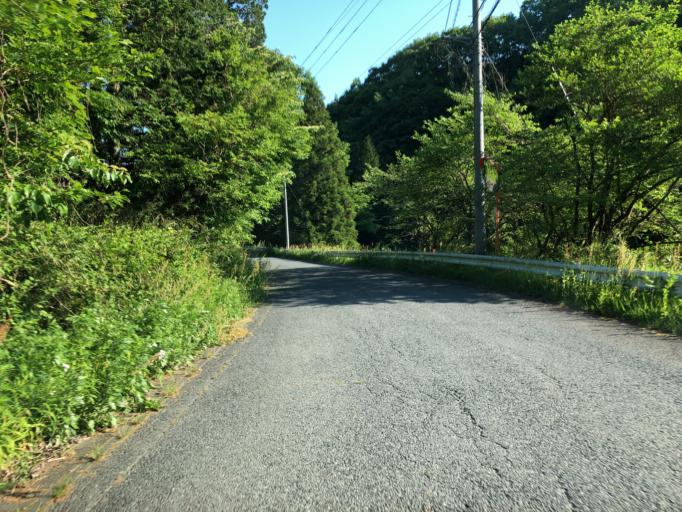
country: JP
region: Ibaraki
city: Kitaibaraki
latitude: 36.8756
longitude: 140.6534
